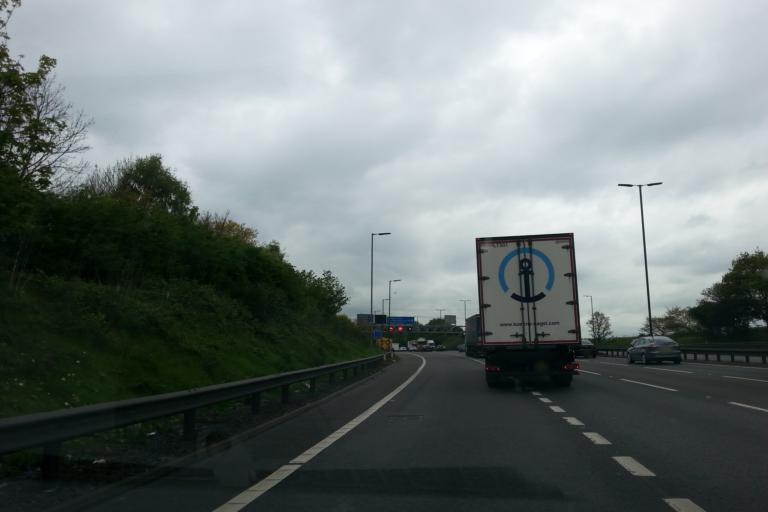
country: GB
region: England
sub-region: City and Borough of Birmingham
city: Hockley
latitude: 52.5513
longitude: -1.9244
